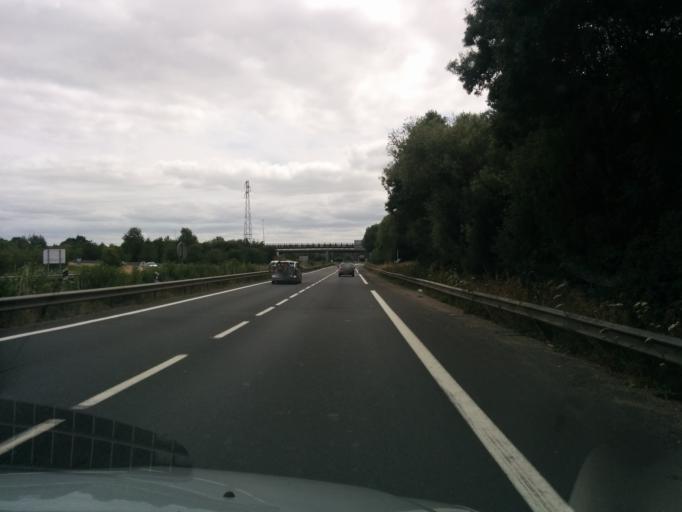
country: FR
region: Pays de la Loire
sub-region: Departement de la Loire-Atlantique
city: Basse-Goulaine
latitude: 47.2205
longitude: -1.4566
